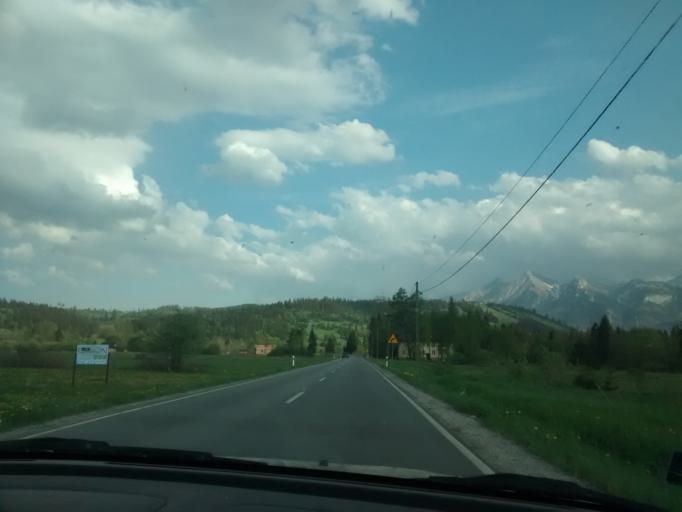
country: PL
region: Lesser Poland Voivodeship
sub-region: Powiat tatrzanski
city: Bukowina Tatrzanska
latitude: 49.3313
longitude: 20.1489
